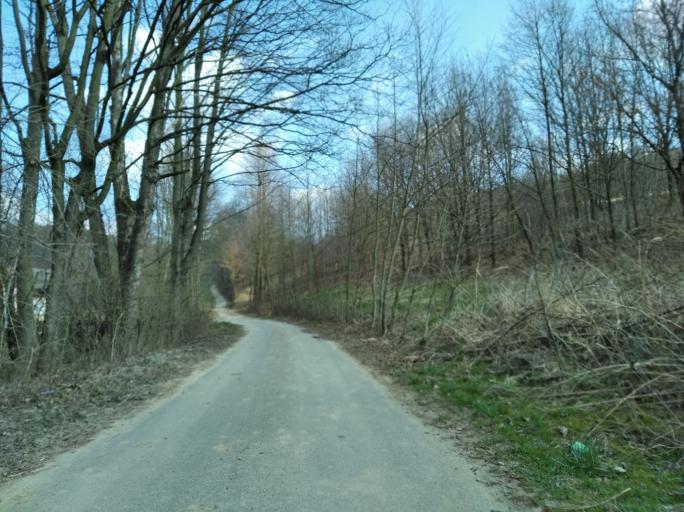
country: PL
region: Subcarpathian Voivodeship
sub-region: Powiat strzyzowski
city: Strzyzow
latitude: 49.8411
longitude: 21.8374
